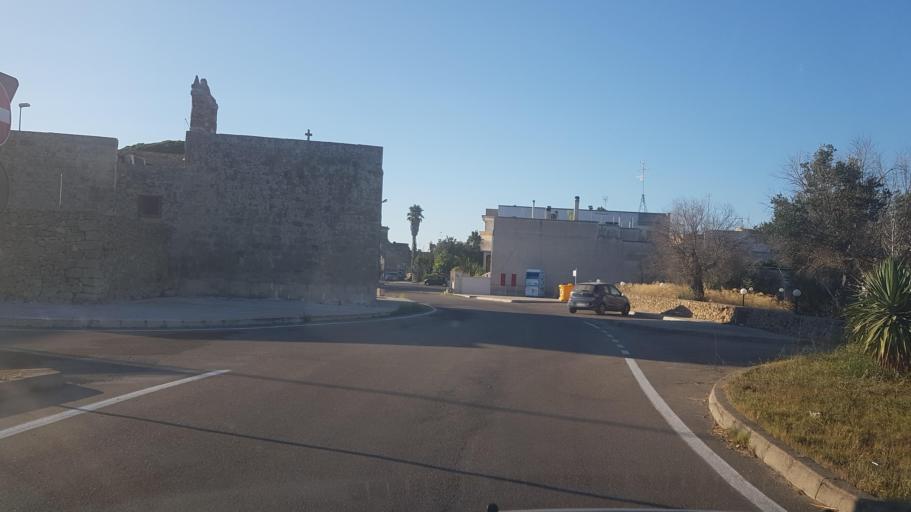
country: IT
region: Apulia
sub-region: Provincia di Lecce
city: Struda
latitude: 40.3322
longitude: 18.2973
